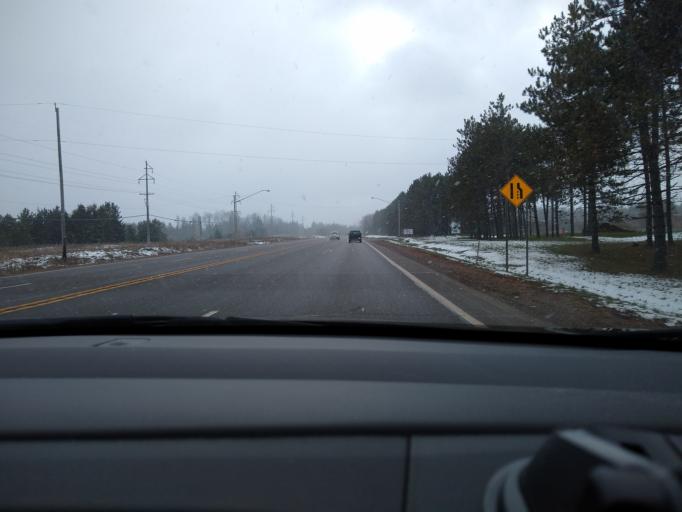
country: US
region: Michigan
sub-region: Dickinson County
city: Iron Mountain
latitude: 46.0397
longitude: -88.0608
